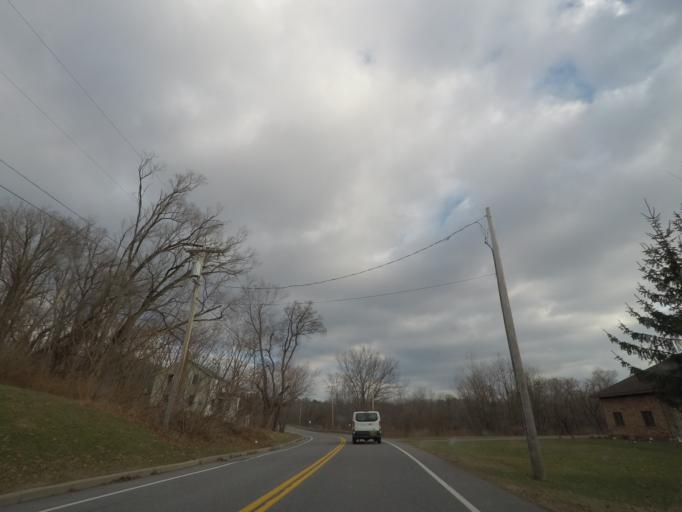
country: US
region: New York
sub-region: Albany County
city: Westmere
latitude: 42.6696
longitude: -73.8841
